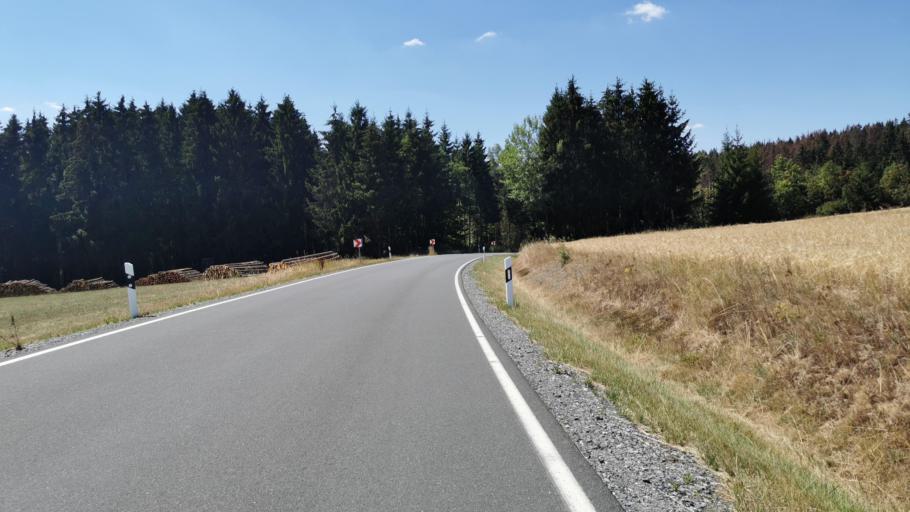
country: DE
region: Bavaria
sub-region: Upper Franconia
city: Teuschnitz
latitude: 50.4258
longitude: 11.3198
